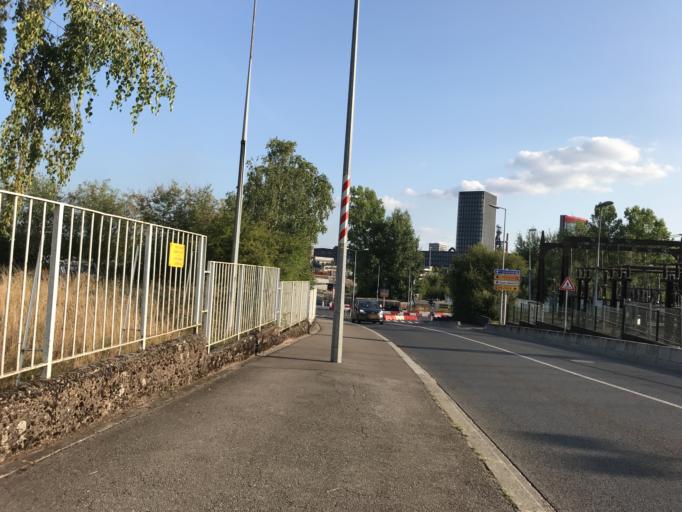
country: LU
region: Luxembourg
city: Soleuvre
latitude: 49.5096
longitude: 5.9486
